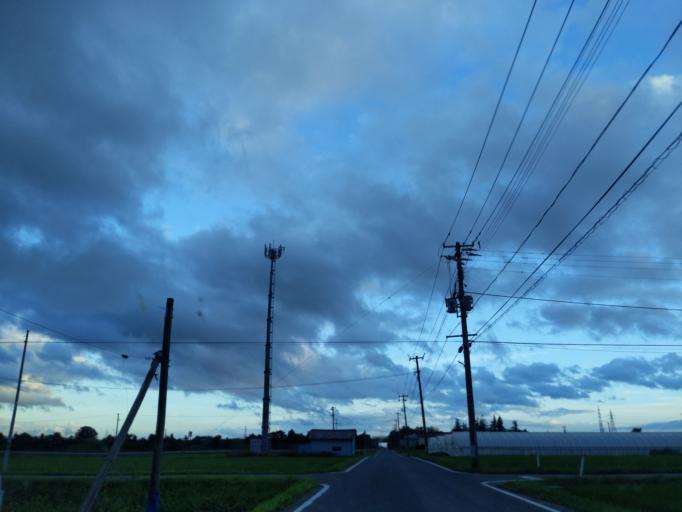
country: JP
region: Fukushima
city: Motomiya
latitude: 37.4652
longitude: 140.3696
